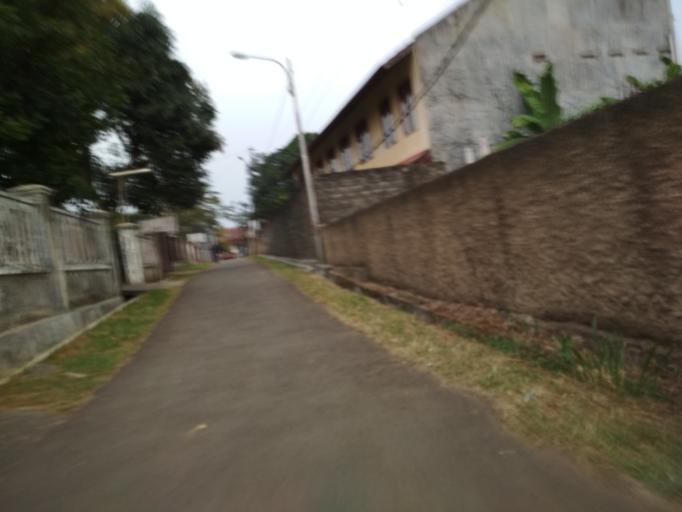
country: ID
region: West Java
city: Ciampea
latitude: -6.5576
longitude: 106.7374
